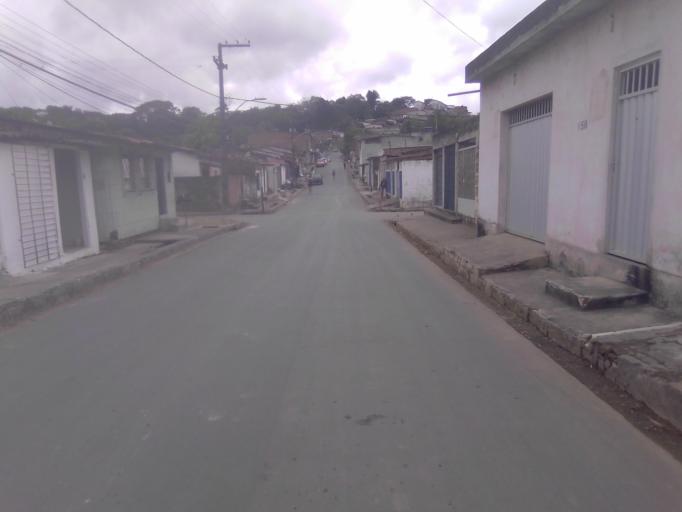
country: BR
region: Pernambuco
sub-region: Jaboatao Dos Guararapes
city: Jaboatao dos Guararapes
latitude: -8.0662
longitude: -35.0020
